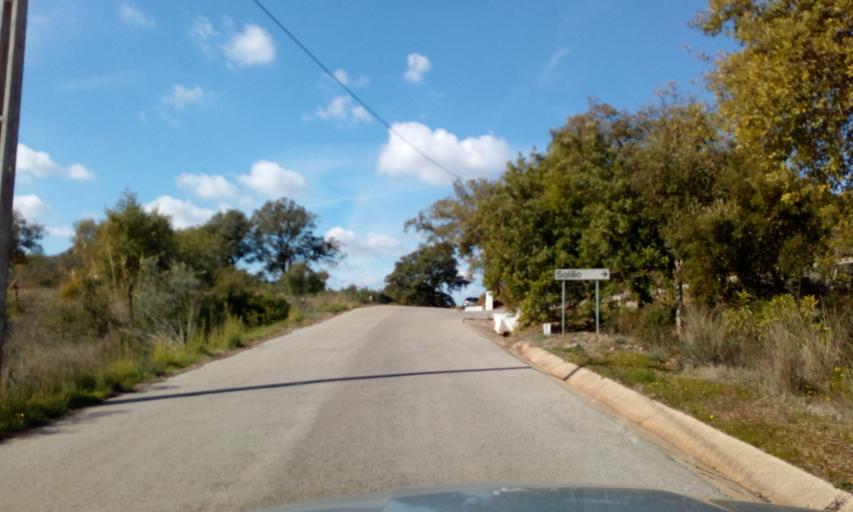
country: PT
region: Faro
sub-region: Loule
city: Loule
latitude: 37.2468
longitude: -8.0839
